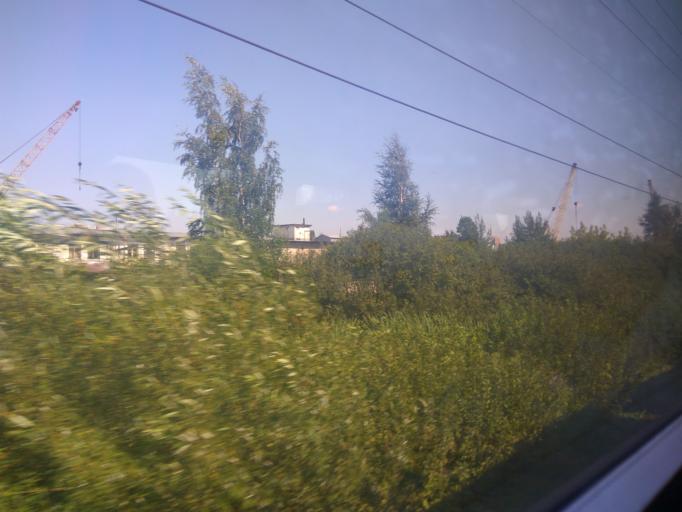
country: RU
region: Moskovskaya
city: Odintsovo
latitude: 55.6678
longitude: 37.2447
